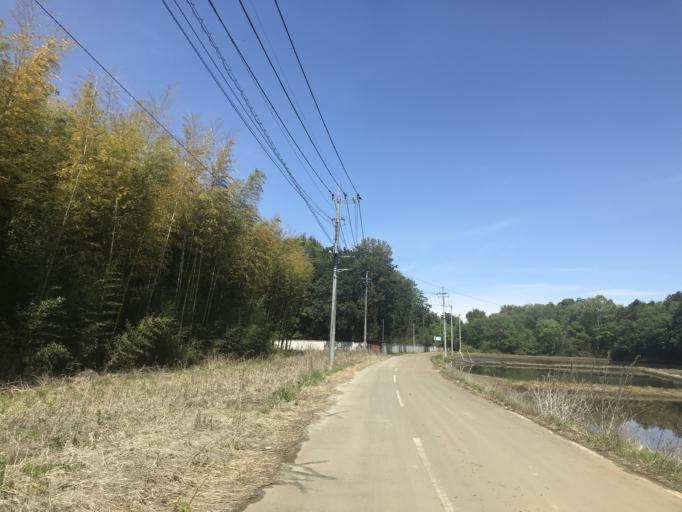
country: JP
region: Ibaraki
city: Shimodate
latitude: 36.2847
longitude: 140.0216
